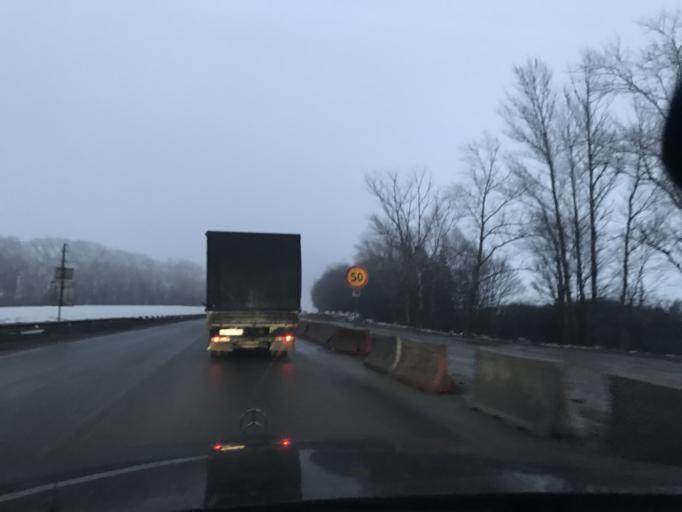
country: RU
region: Vladimir
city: Novovyazniki
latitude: 56.2165
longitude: 42.2425
